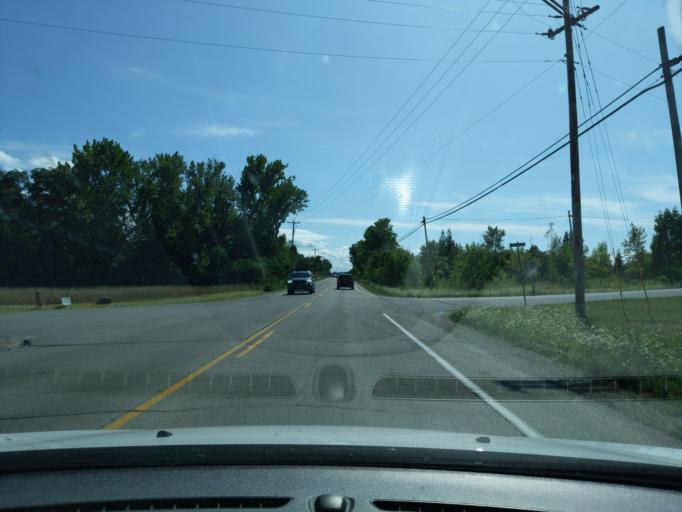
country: US
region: Wisconsin
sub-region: Door County
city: Sturgeon Bay
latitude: 45.2150
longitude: -87.1117
